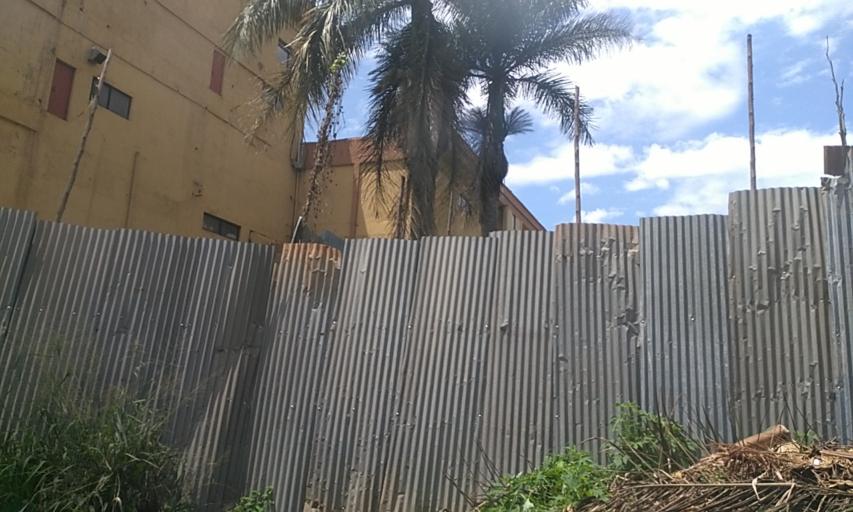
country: UG
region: Central Region
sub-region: Kampala District
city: Kampala
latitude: 0.3187
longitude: 32.5932
